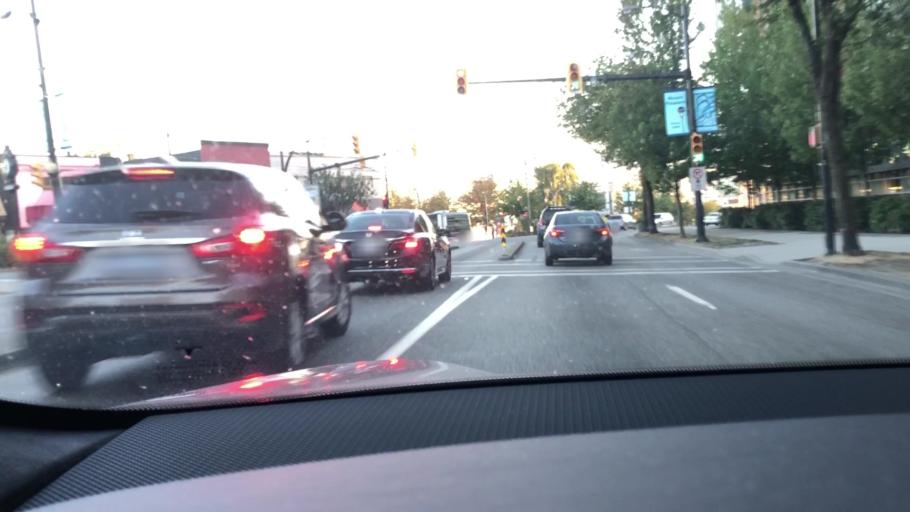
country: CA
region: British Columbia
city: Vancouver
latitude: 49.2639
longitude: -123.1005
